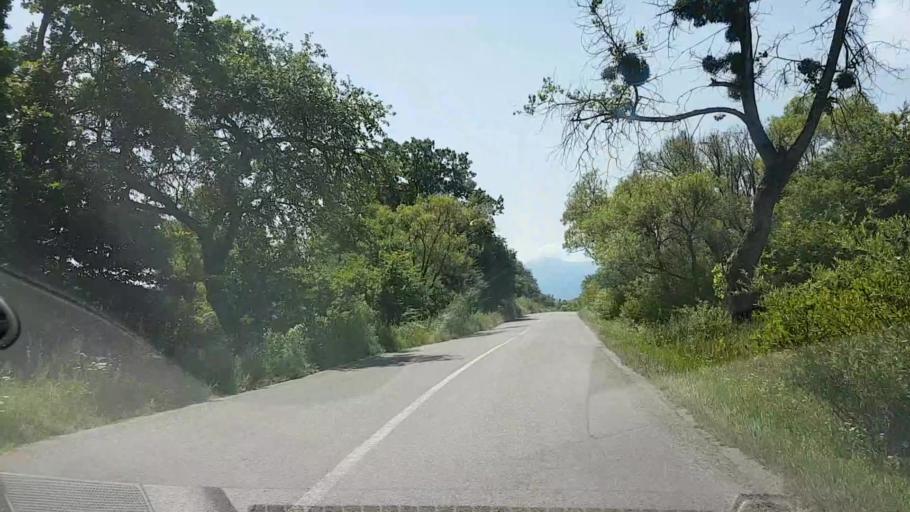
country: RO
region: Brasov
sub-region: Comuna Voila
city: Voila
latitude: 45.8661
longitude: 24.8248
